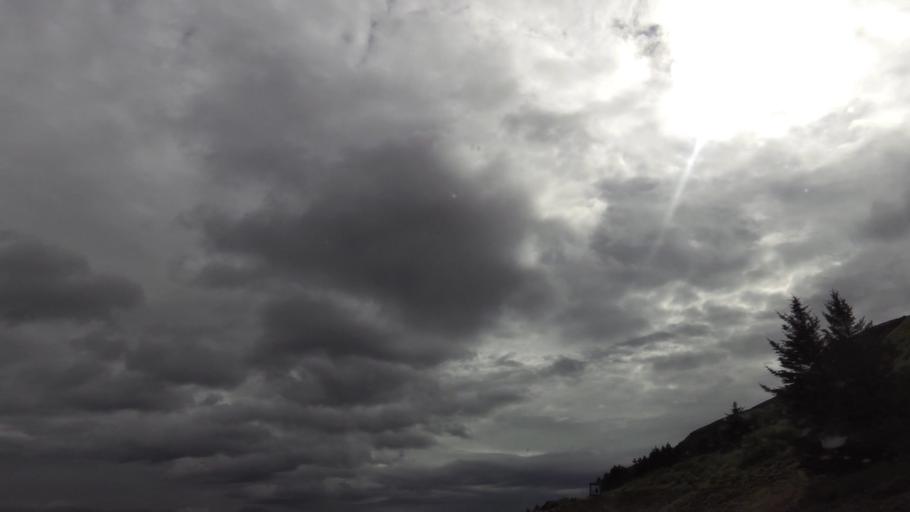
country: IS
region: West
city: Stykkisholmur
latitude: 65.5132
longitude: -22.1107
